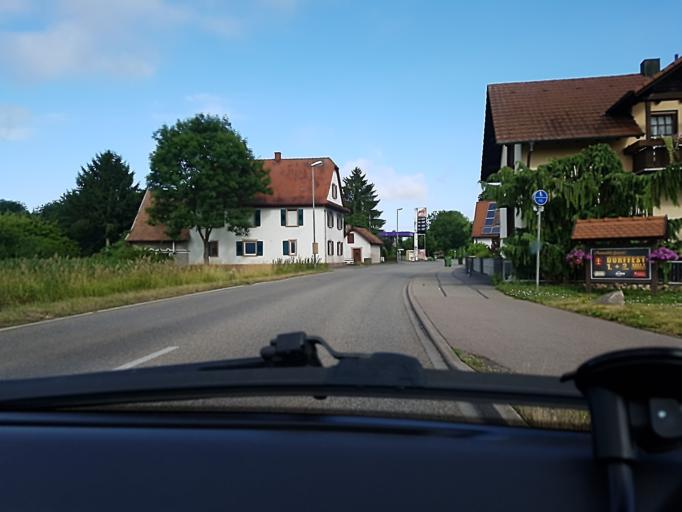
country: DE
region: Baden-Wuerttemberg
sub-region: Freiburg Region
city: Kehl
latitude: 48.5673
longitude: 7.8531
